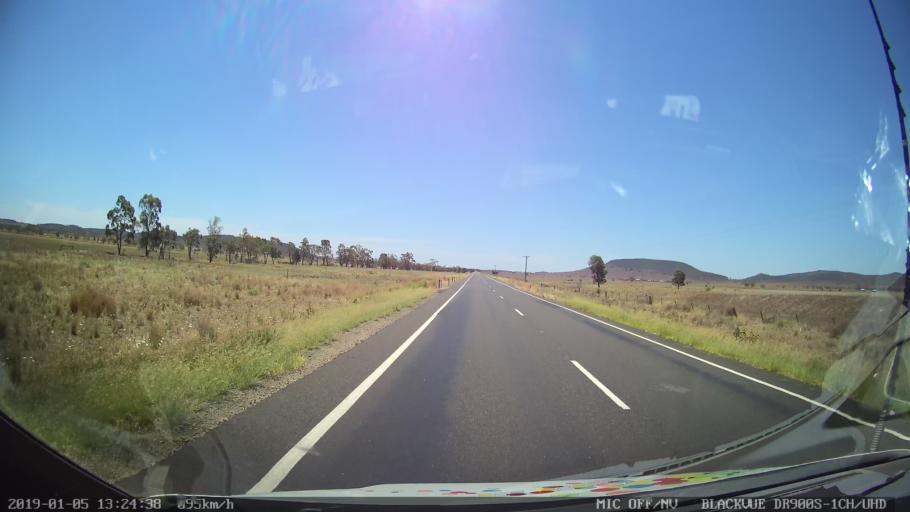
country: AU
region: New South Wales
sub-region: Gunnedah
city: Gunnedah
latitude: -31.0678
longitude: 149.9916
